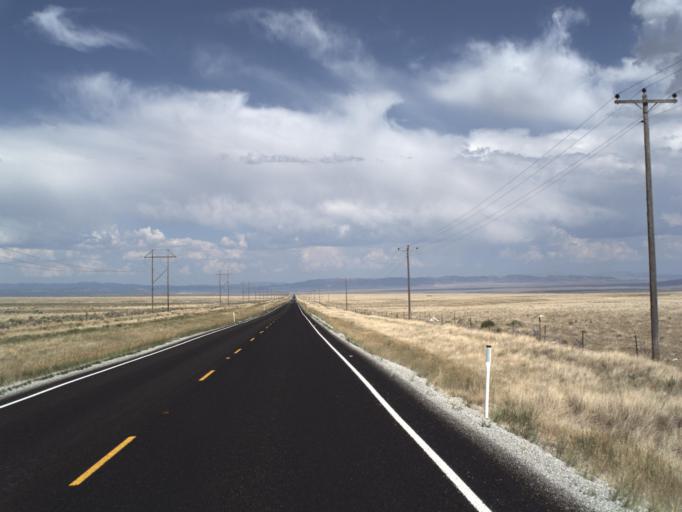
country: US
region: Idaho
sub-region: Minidoka County
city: Rupert
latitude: 41.9714
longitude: -113.1387
